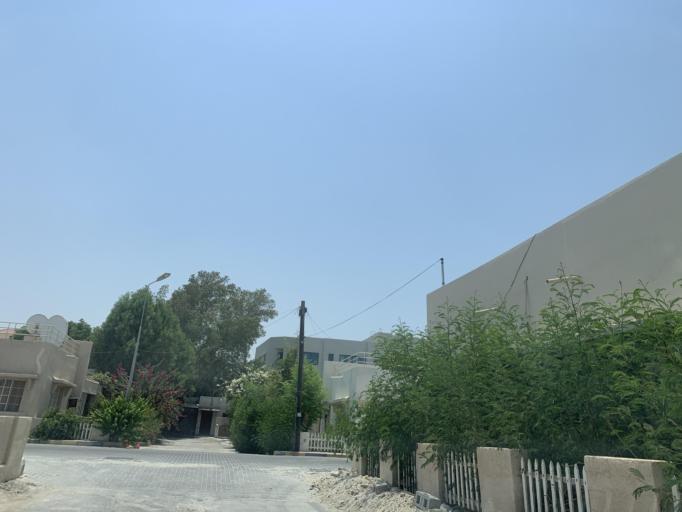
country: BH
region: Manama
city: Jidd Hafs
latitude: 26.2171
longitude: 50.5618
